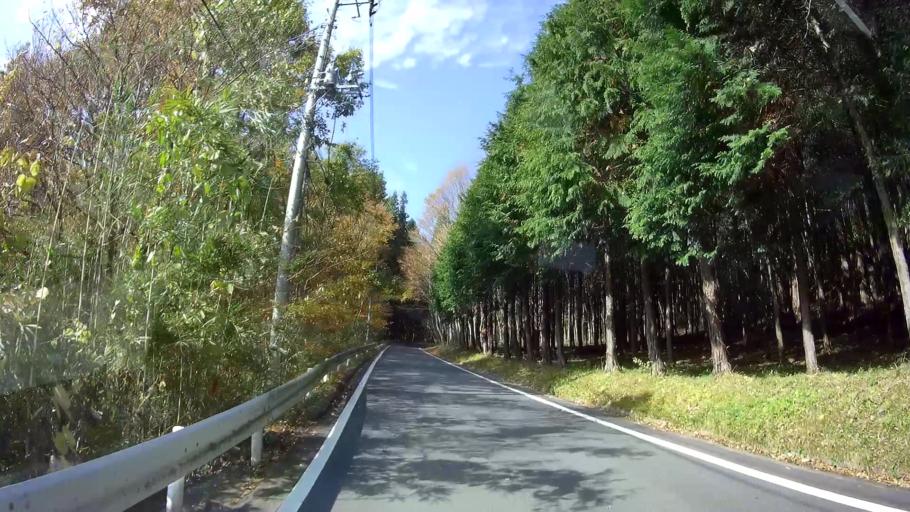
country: JP
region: Gunma
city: Nakanojomachi
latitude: 36.5046
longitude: 138.6789
